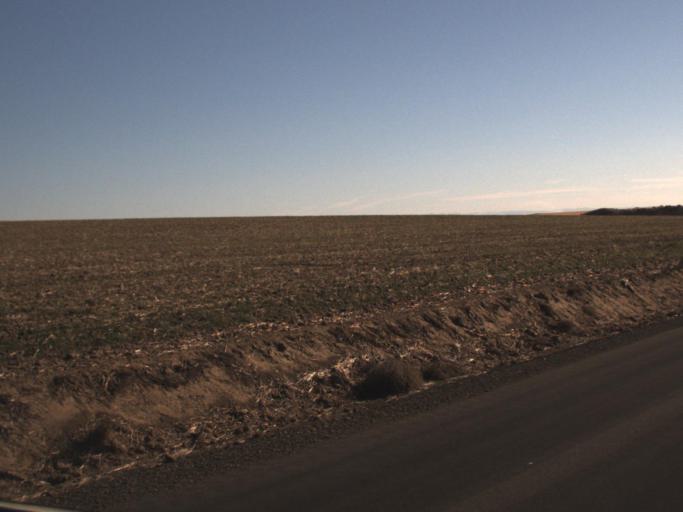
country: US
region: Washington
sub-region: Franklin County
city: Connell
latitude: 46.7902
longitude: -118.5473
